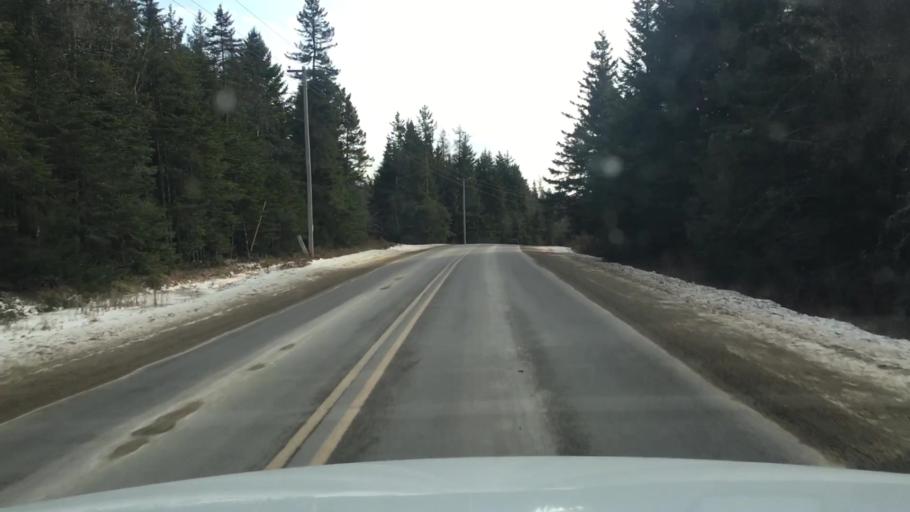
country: US
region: Maine
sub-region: Washington County
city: Jonesport
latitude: 44.6374
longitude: -67.5932
